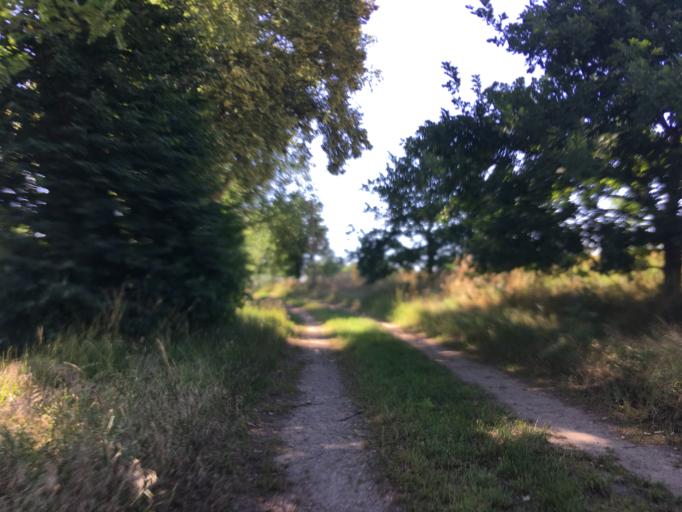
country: DE
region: Brandenburg
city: Brussow
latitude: 53.3257
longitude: 14.0868
